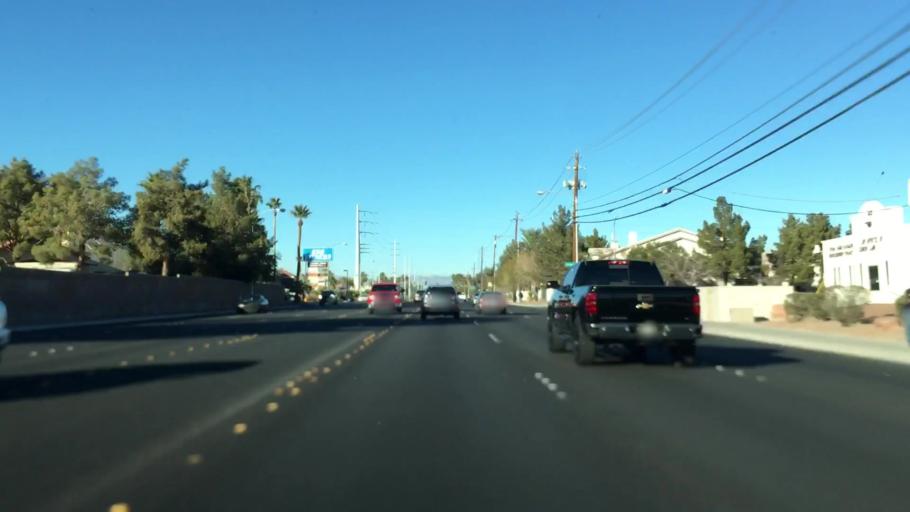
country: US
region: Nevada
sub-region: Clark County
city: Whitney
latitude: 36.0837
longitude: -115.1010
